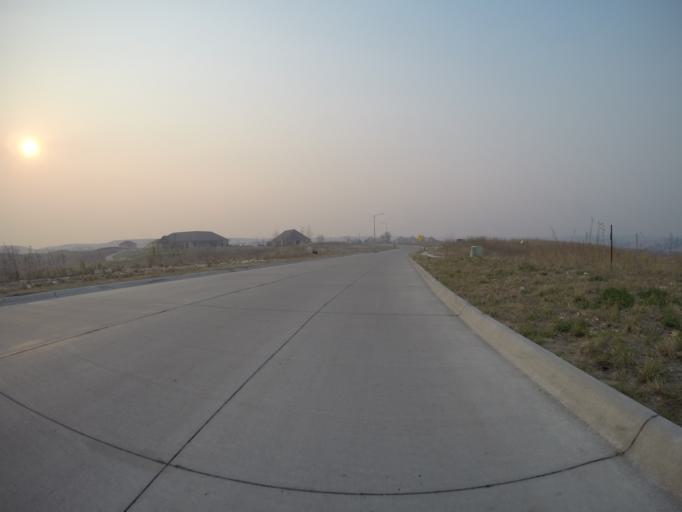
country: US
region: Kansas
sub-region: Riley County
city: Manhattan
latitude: 39.2120
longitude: -96.6386
